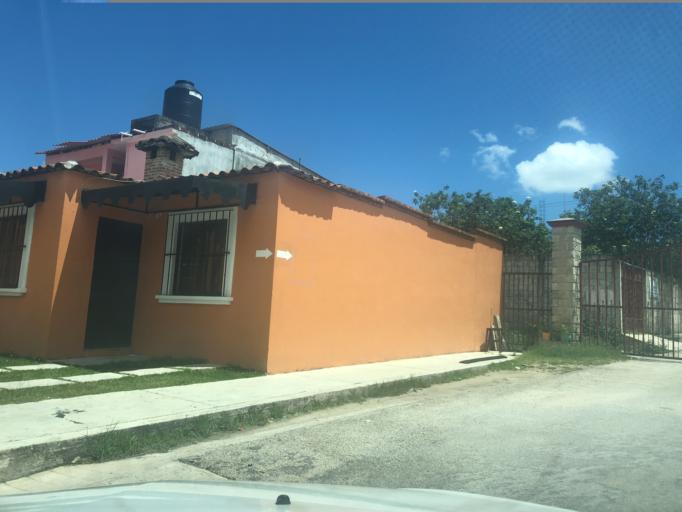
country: MX
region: Chiapas
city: San Cristobal de las Casas
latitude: 16.7176
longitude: -92.6449
